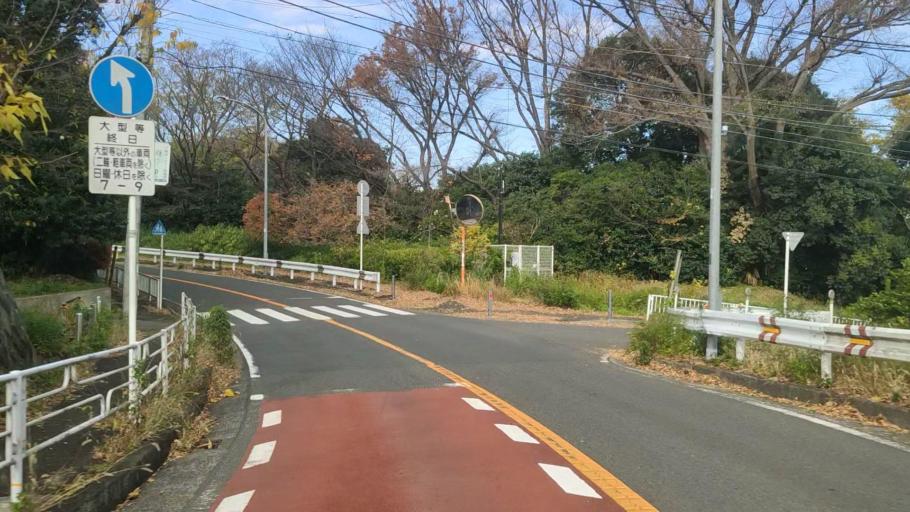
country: JP
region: Kanagawa
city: Minami-rinkan
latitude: 35.4536
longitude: 139.5392
